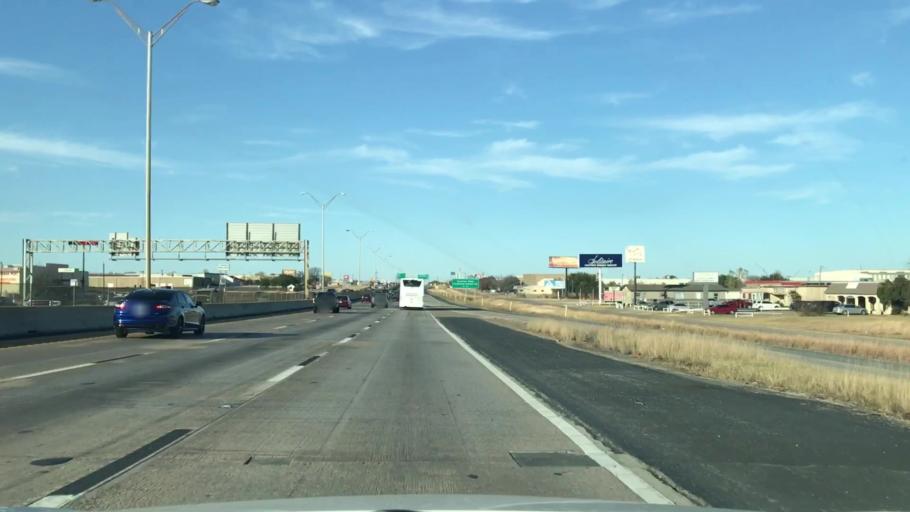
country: US
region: Texas
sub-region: Tarrant County
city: Everman
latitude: 32.6178
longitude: -97.3212
